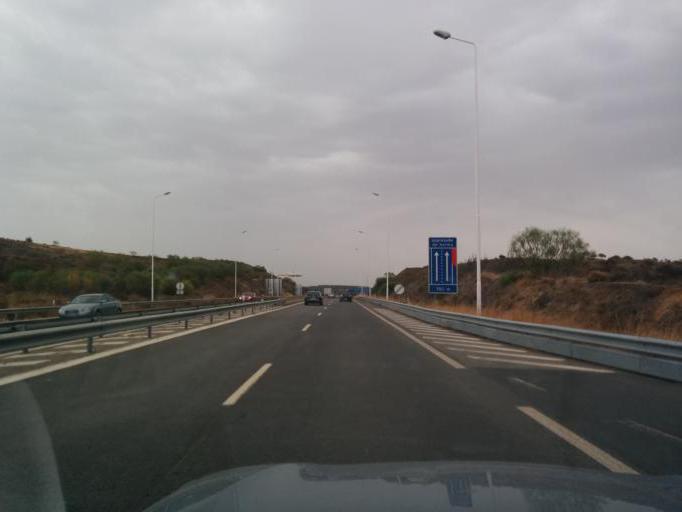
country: PT
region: Faro
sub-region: Castro Marim
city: Castro Marim
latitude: 37.2366
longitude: -7.4368
